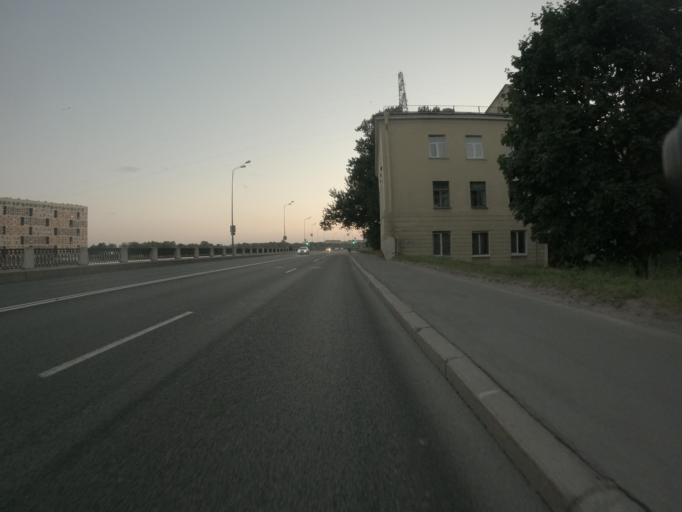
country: RU
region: St.-Petersburg
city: Obukhovo
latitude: 59.8717
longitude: 30.4665
